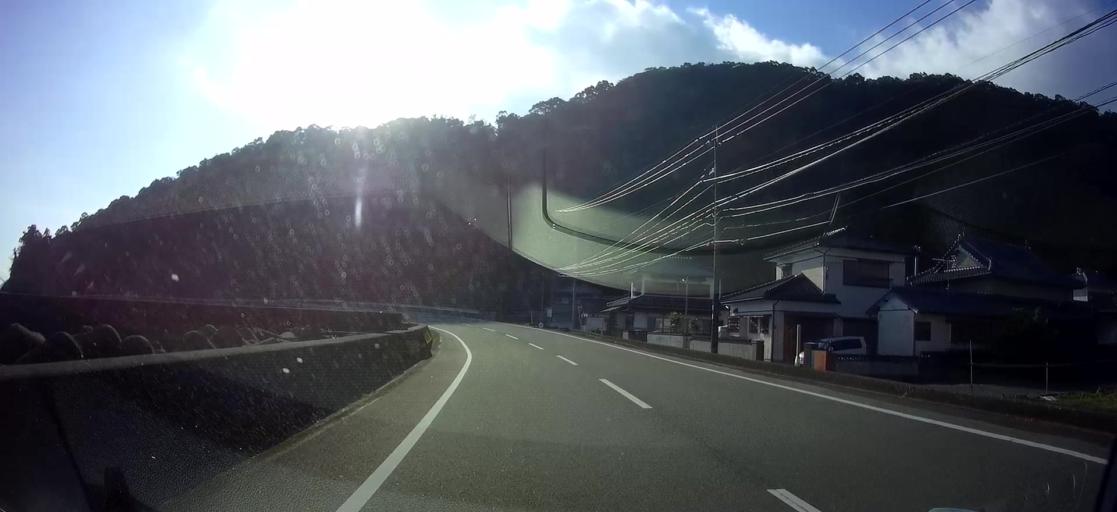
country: JP
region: Kumamoto
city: Minamata
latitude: 32.3877
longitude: 130.3823
